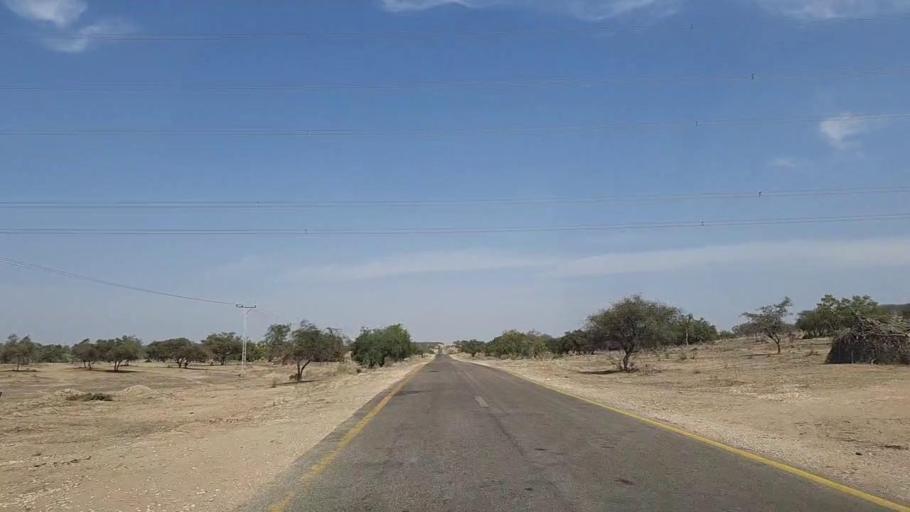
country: PK
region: Sindh
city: Mithi
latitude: 24.8523
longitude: 69.8384
